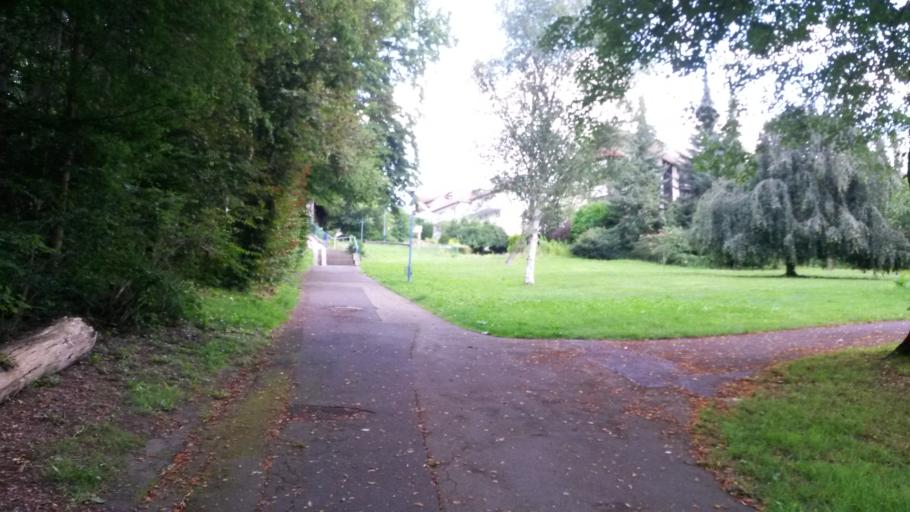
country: DE
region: Baden-Wuerttemberg
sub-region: Karlsruhe Region
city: Ettlingen
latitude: 48.9219
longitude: 8.4717
